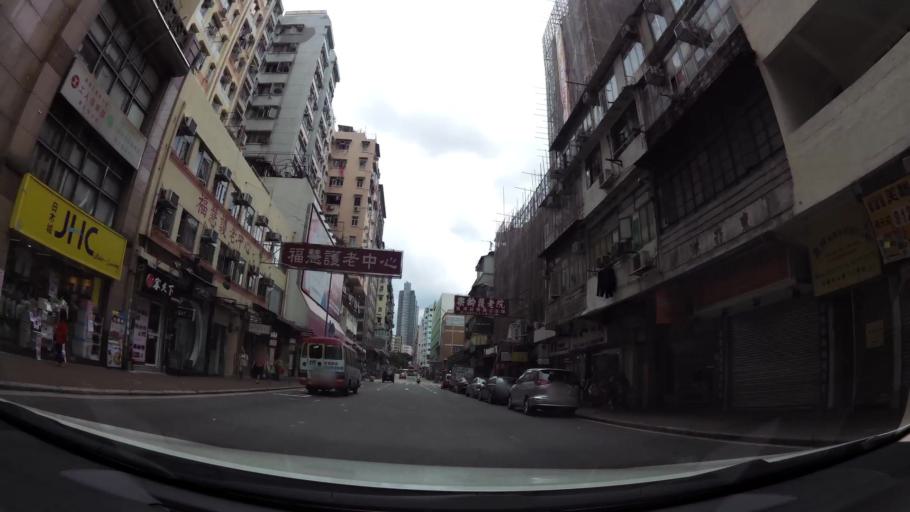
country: HK
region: Sham Shui Po
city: Sham Shui Po
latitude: 22.3348
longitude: 114.1611
